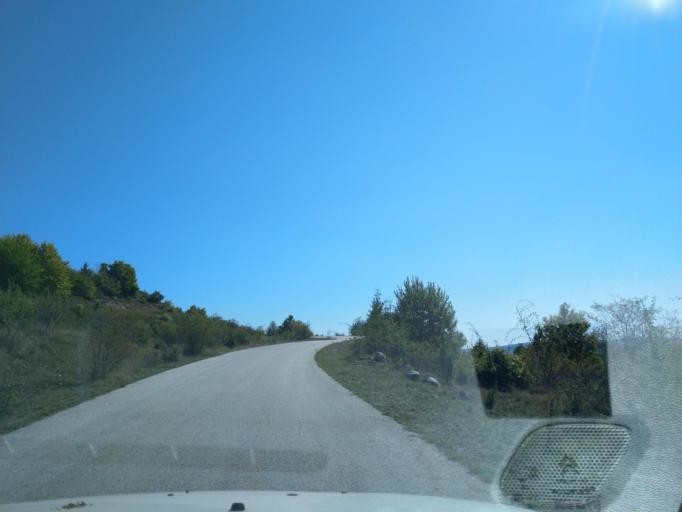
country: RS
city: Sokolovica
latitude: 43.2517
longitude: 20.3098
